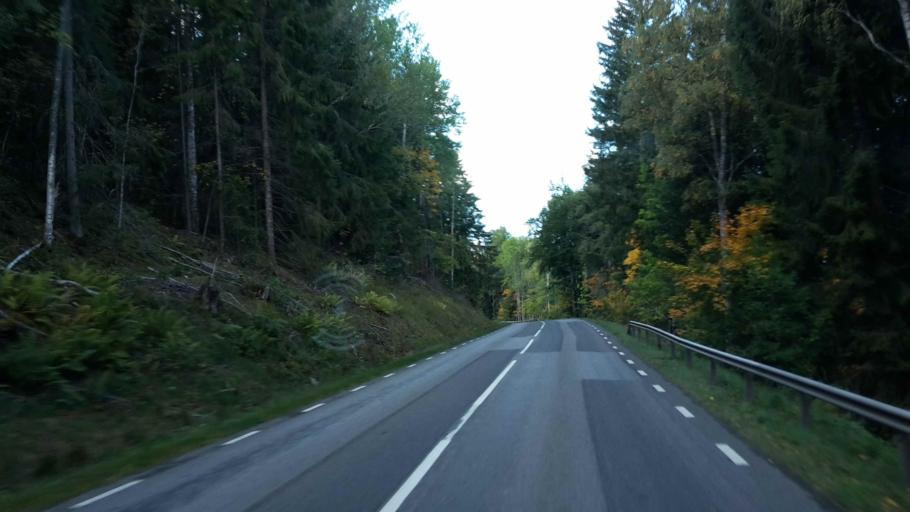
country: SE
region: OEstergoetland
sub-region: Atvidabergs Kommun
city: Atvidaberg
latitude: 58.1752
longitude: 16.1285
